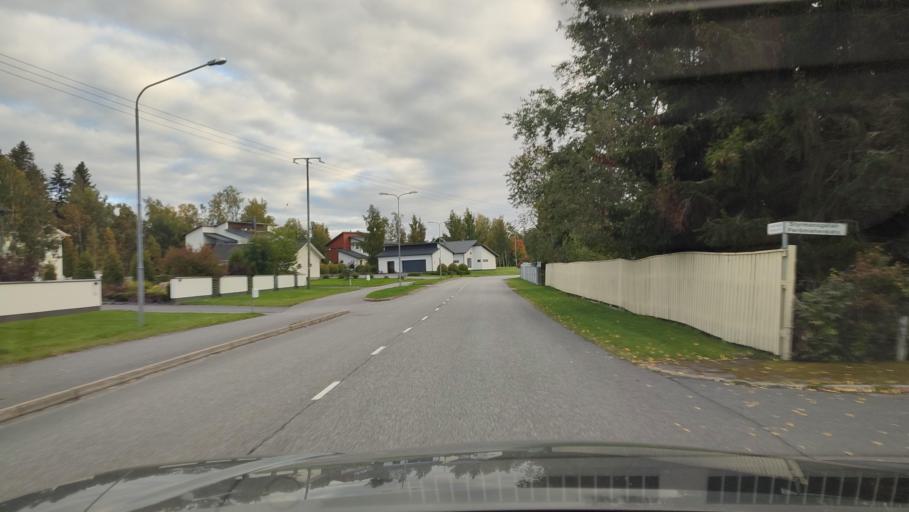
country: FI
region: Ostrobothnia
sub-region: Sydosterbotten
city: Kristinestad
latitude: 62.2705
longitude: 21.3876
